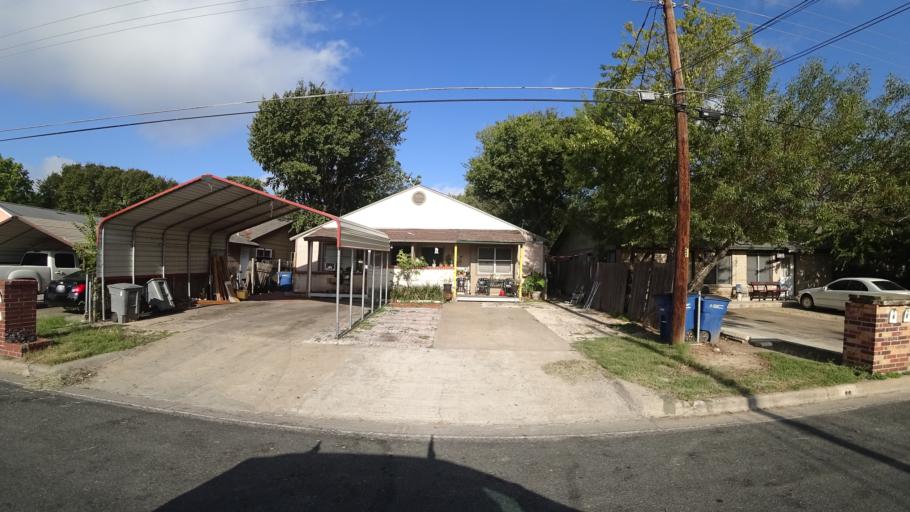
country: US
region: Texas
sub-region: Travis County
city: Austin
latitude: 30.3265
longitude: -97.6978
